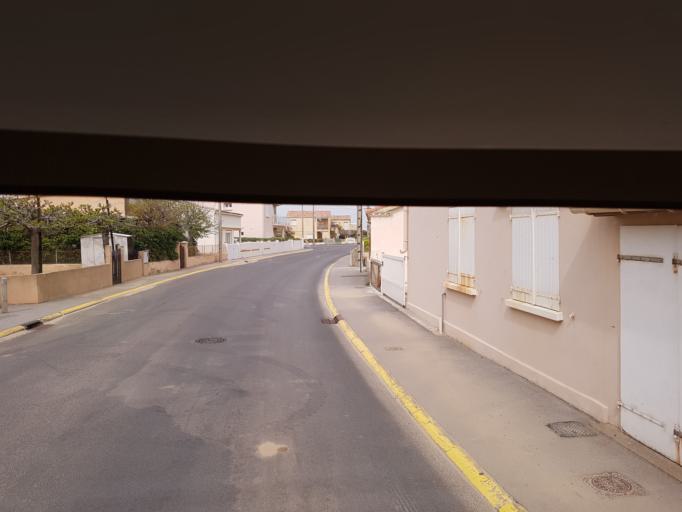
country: FR
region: Languedoc-Roussillon
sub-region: Departement de l'Aude
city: Fleury
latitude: 43.1617
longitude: 3.1705
